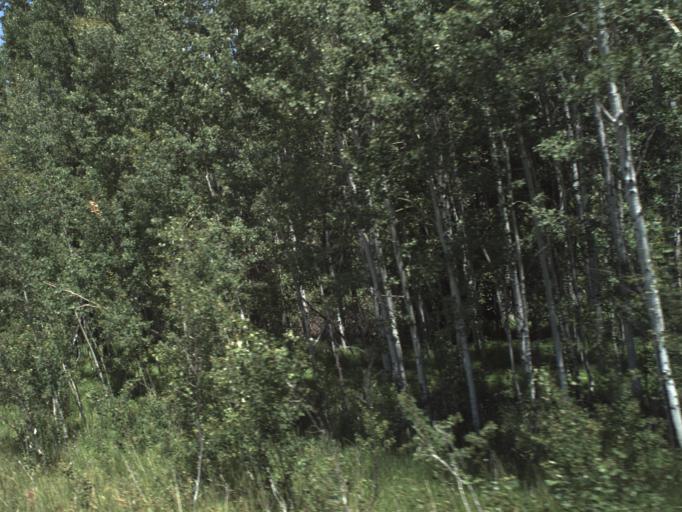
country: US
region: Utah
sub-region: Weber County
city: Wolf Creek
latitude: 41.3125
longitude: -111.6153
